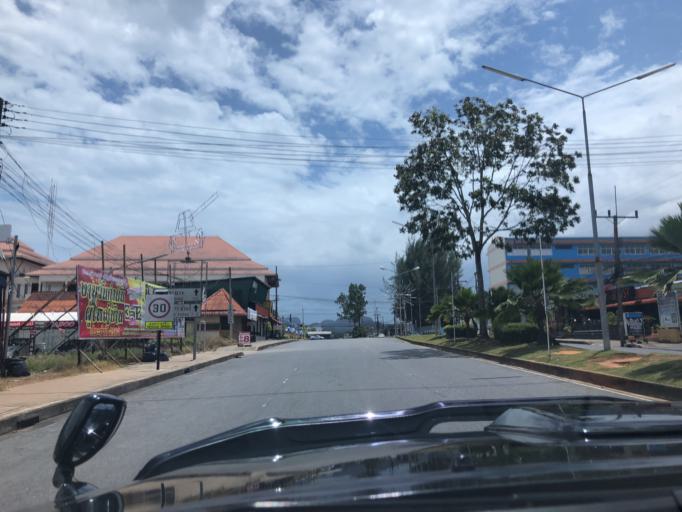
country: TH
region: Krabi
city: Krabi
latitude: 8.0854
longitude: 98.9083
